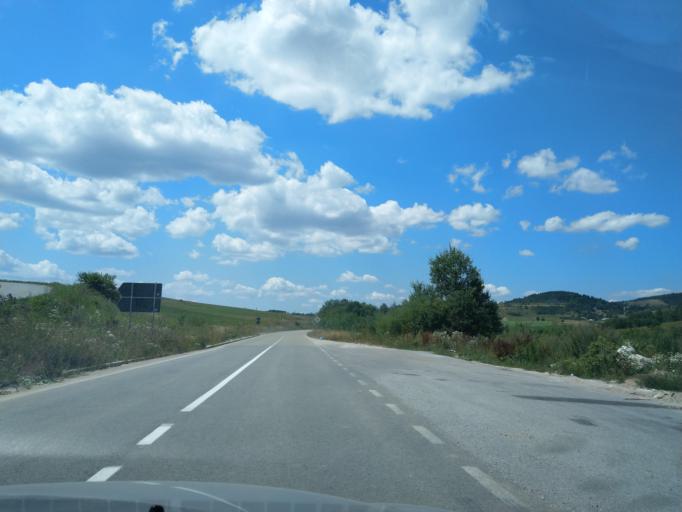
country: RS
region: Central Serbia
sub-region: Zlatiborski Okrug
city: Sjenica
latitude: 43.3292
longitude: 19.8789
